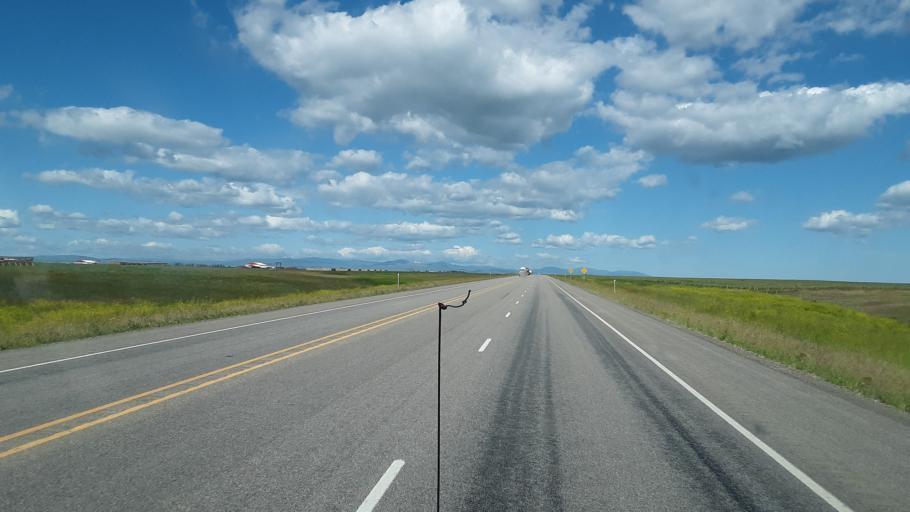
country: US
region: Montana
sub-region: Fergus County
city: Lewistown
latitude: 46.9985
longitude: -109.8126
